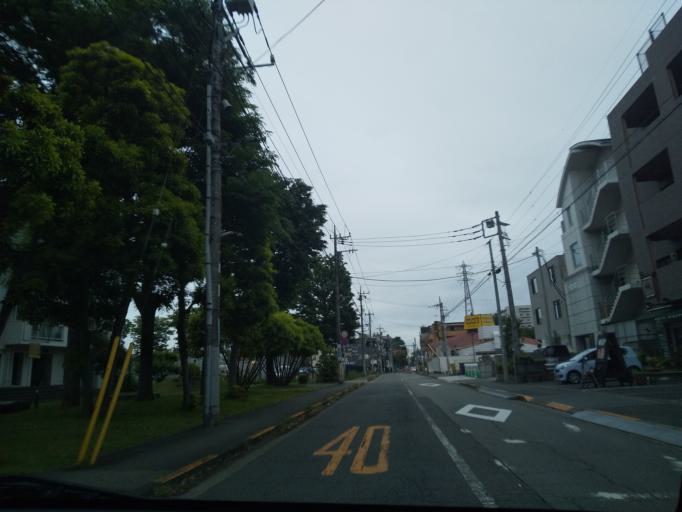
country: JP
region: Tokyo
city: Hino
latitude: 35.6634
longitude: 139.3780
